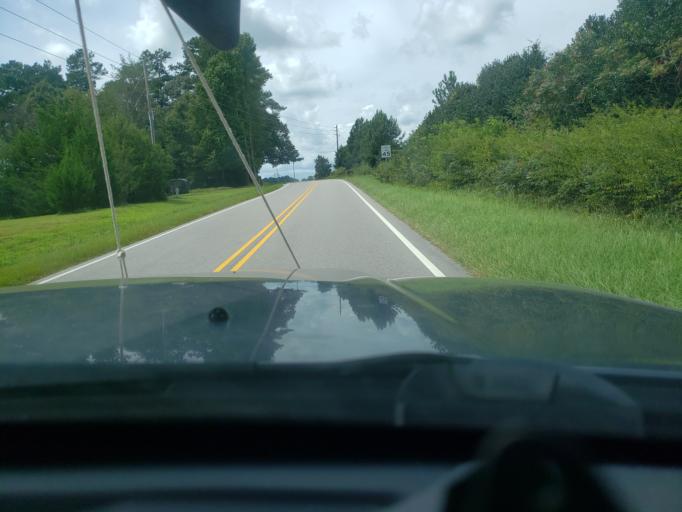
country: US
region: North Carolina
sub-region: Wake County
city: Rolesville
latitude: 35.8820
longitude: -78.3909
